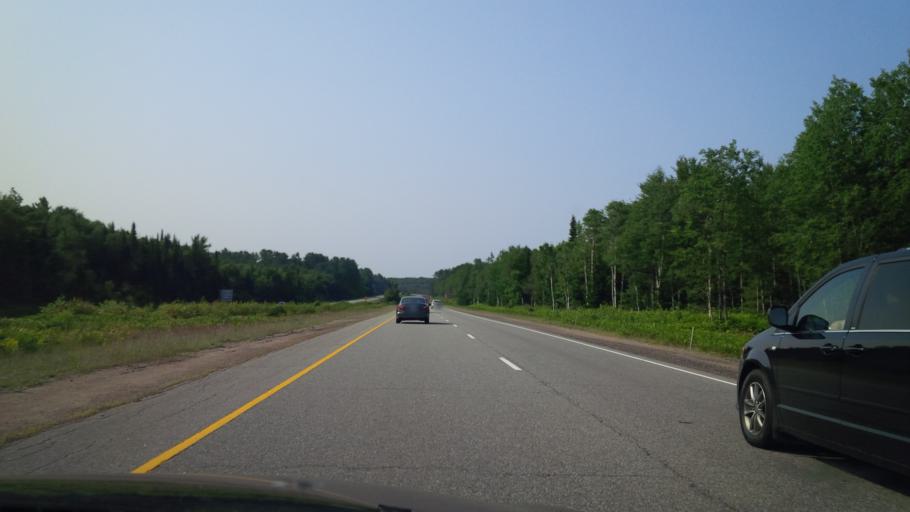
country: CA
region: Ontario
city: Bracebridge
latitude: 45.1194
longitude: -79.3110
